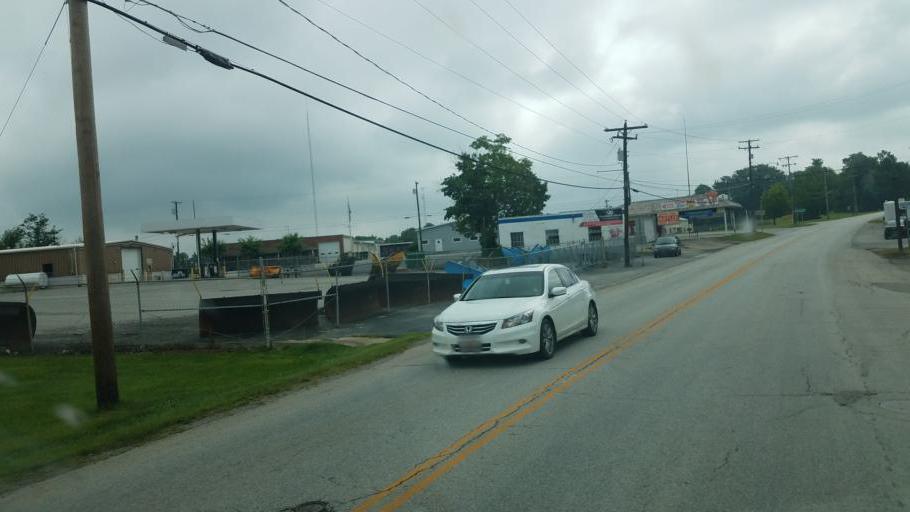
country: US
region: Ohio
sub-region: Highland County
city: Hillsboro
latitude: 39.2003
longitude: -83.5999
